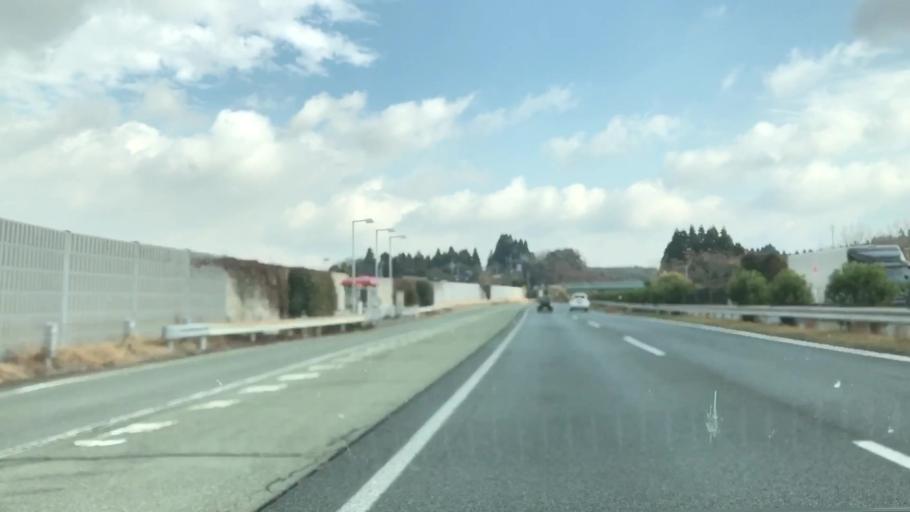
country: JP
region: Fukuoka
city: Omuta
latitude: 33.0440
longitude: 130.5637
